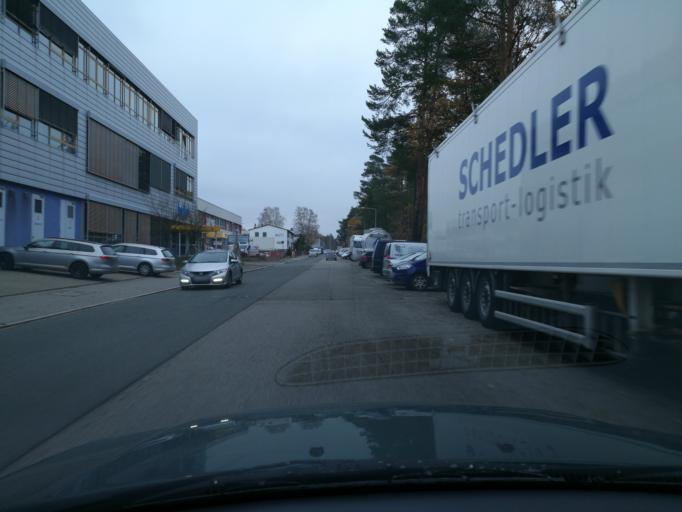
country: DE
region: Bavaria
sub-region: Regierungsbezirk Mittelfranken
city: Wendelstein
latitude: 49.4131
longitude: 11.1628
